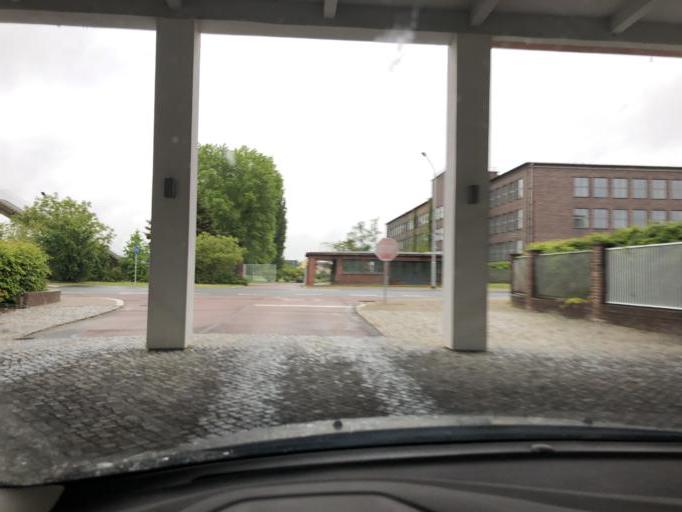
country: DE
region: Saxony-Anhalt
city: Dessau
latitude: 51.8262
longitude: 12.2051
